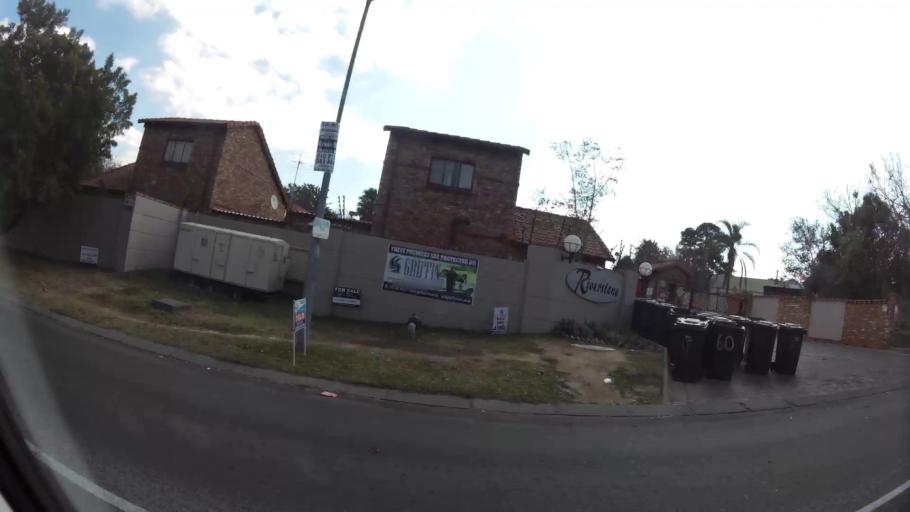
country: ZA
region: Gauteng
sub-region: City of Johannesburg Metropolitan Municipality
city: Midrand
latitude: -25.9930
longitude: 28.1124
